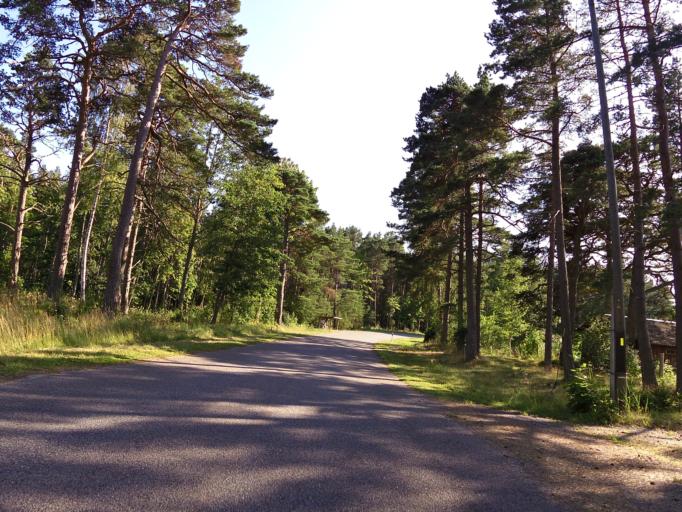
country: EE
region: Hiiumaa
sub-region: Kaerdla linn
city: Kardla
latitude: 58.8926
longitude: 22.2716
